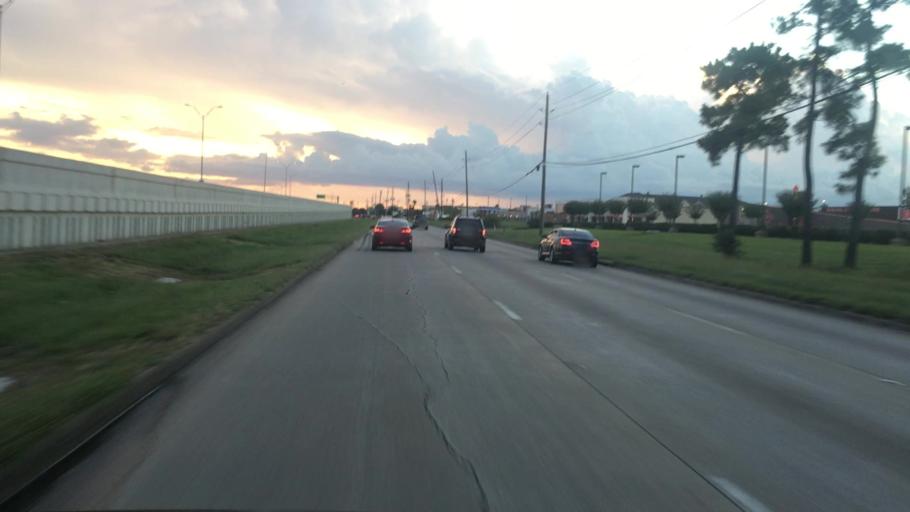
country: US
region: Texas
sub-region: Harris County
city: Humble
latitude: 29.9350
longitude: -95.2398
